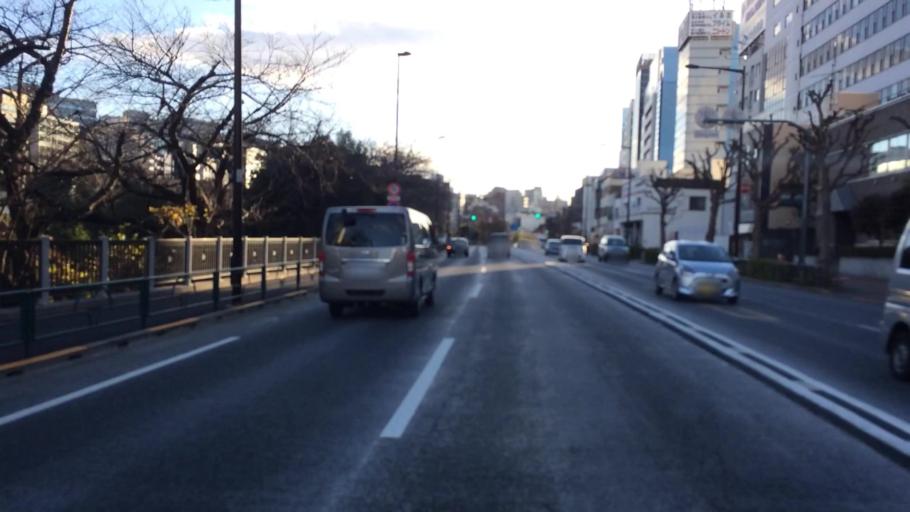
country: JP
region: Tokyo
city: Tokyo
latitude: 35.6967
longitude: 139.7395
